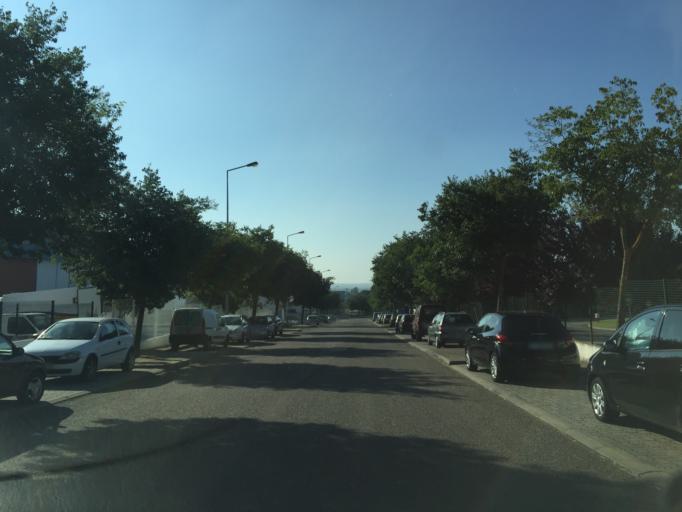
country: PT
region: Santarem
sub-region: Abrantes
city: Alferrarede
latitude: 39.4909
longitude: -8.1850
